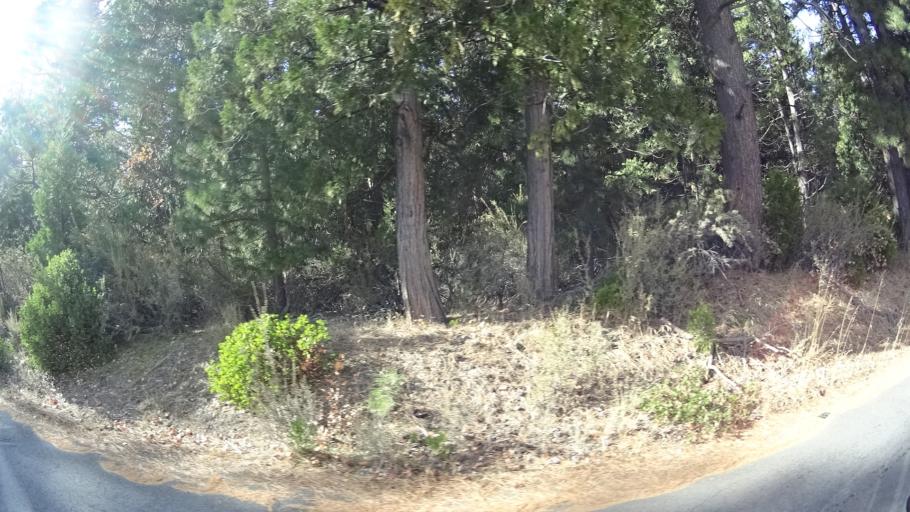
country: US
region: California
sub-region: Siskiyou County
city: Weed
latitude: 41.4279
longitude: -122.3973
